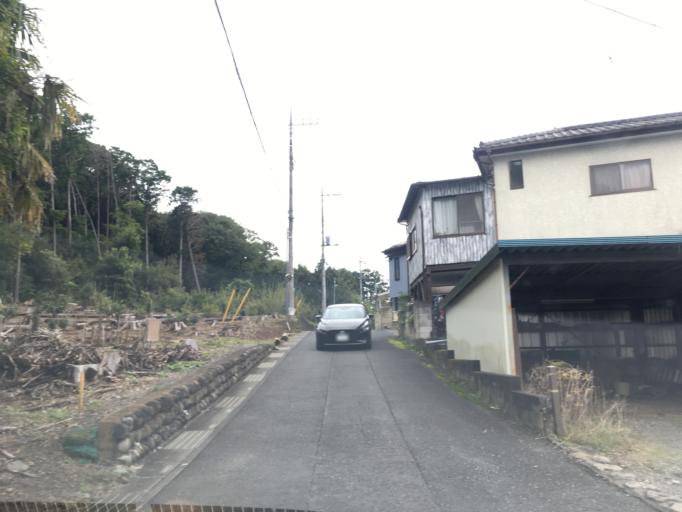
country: JP
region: Saitama
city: Hanno
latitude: 35.8641
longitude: 139.3219
